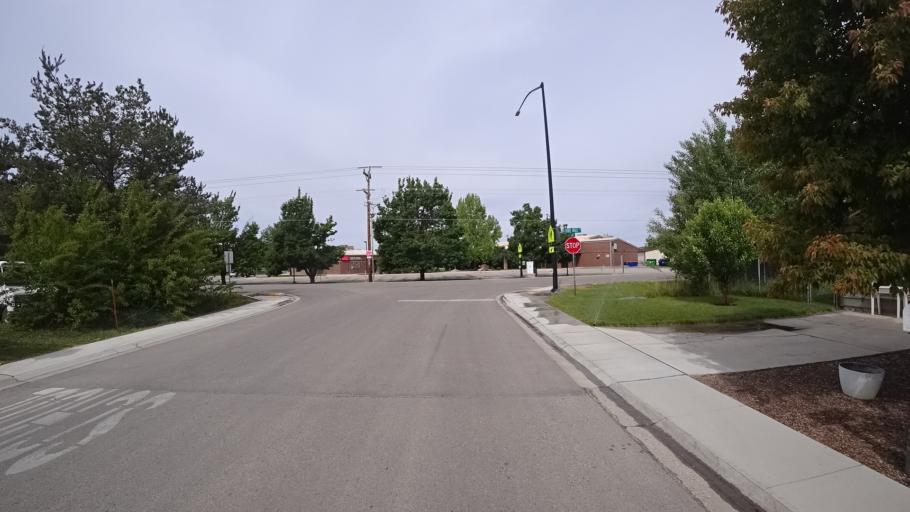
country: US
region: Idaho
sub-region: Ada County
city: Meridian
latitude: 43.5387
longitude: -116.3141
